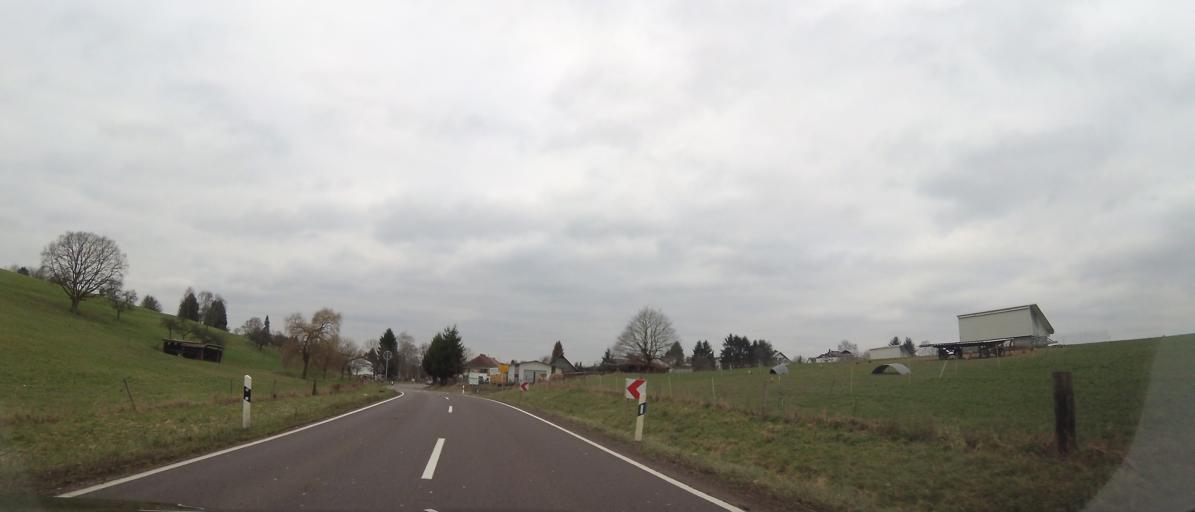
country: DE
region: Saarland
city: Puttlingen
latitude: 49.3092
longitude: 6.8582
